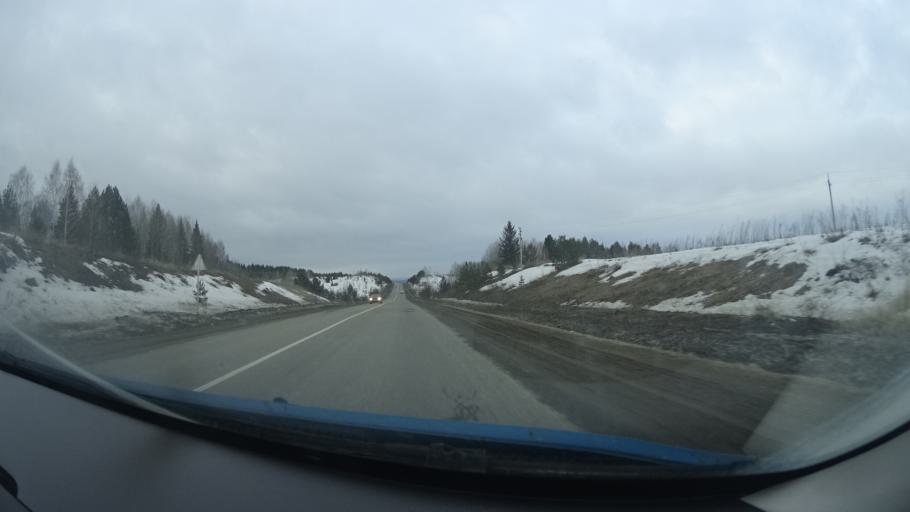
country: RU
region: Perm
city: Osa
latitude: 57.2384
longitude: 55.5961
